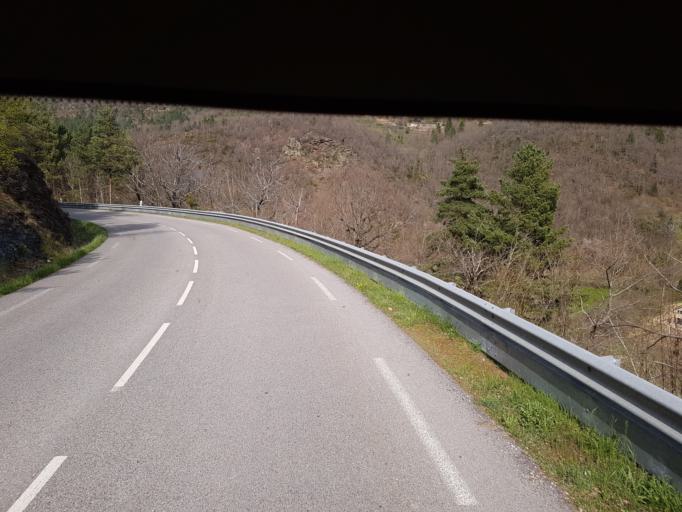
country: FR
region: Languedoc-Roussillon
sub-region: Departement de la Lozere
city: Florac
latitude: 44.3006
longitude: 3.6000
